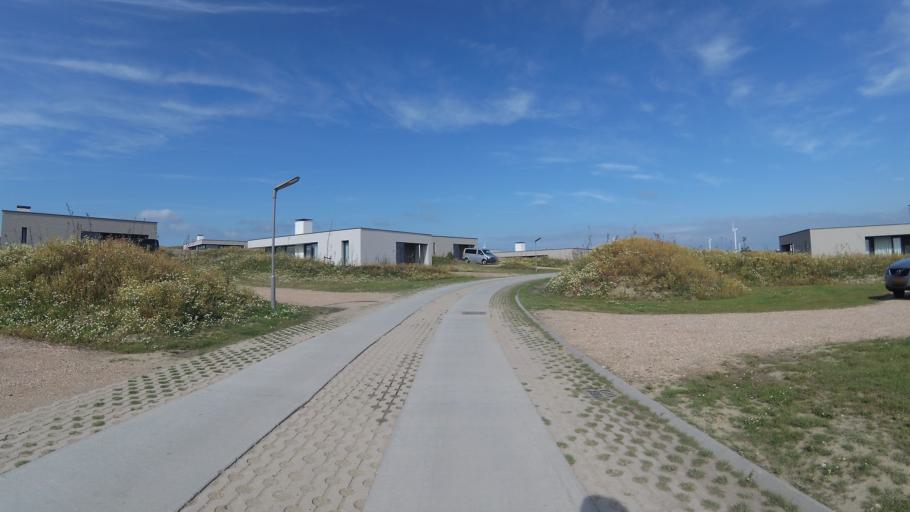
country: NL
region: Zeeland
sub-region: Gemeente Veere
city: Veere
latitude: 51.5871
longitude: 3.6643
